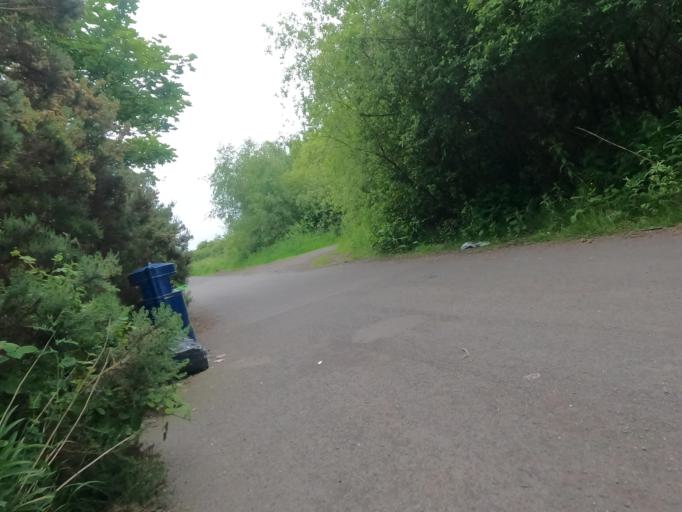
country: GB
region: England
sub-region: Northumberland
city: Bedlington
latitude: 55.1244
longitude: -1.5654
